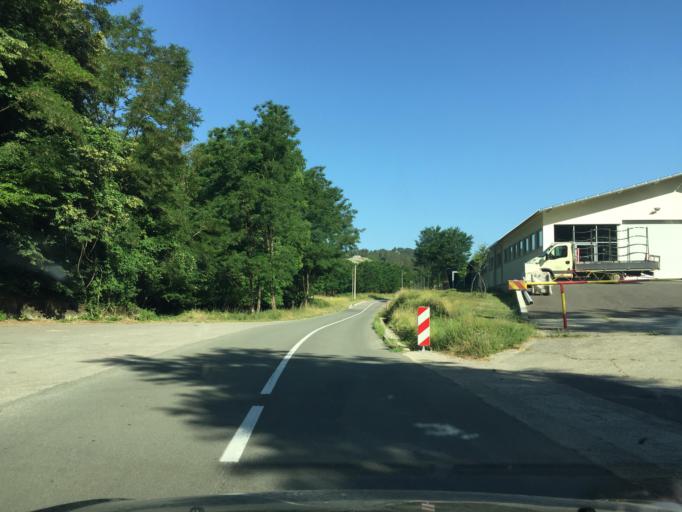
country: HR
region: Primorsko-Goranska
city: Klana
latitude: 45.4419
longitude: 14.3819
